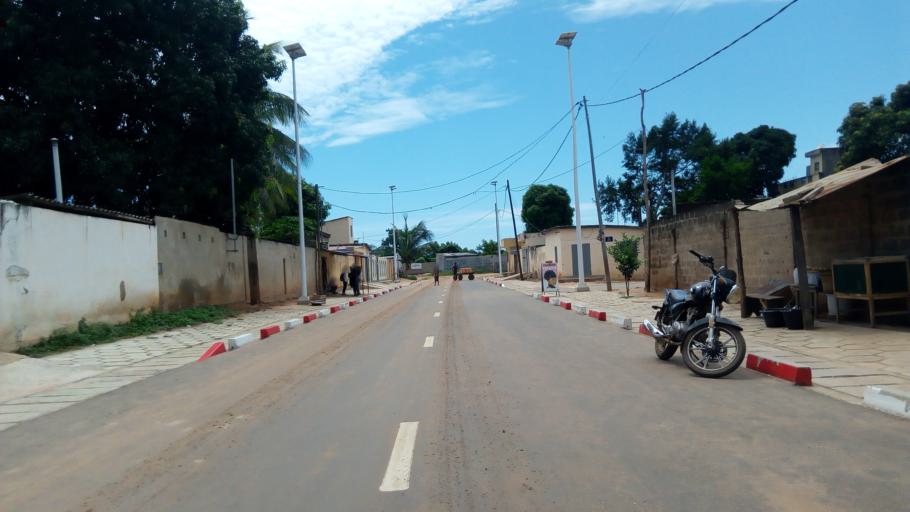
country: TG
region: Maritime
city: Lome
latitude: 6.1708
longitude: 1.1825
